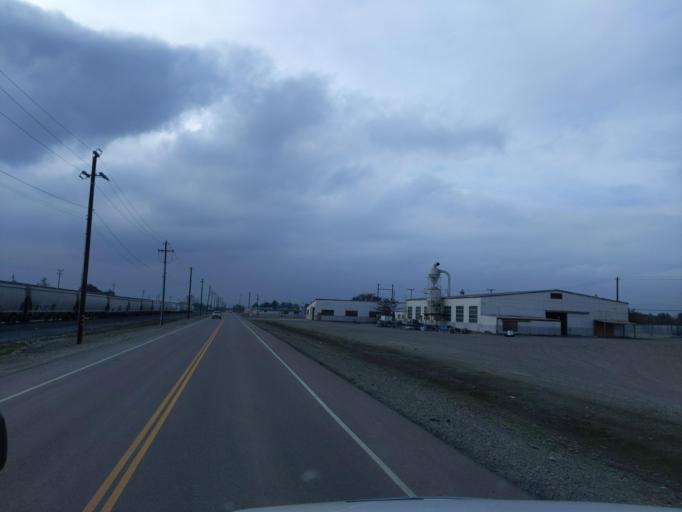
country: US
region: California
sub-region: San Joaquin County
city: Country Club
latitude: 37.9490
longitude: -121.3608
